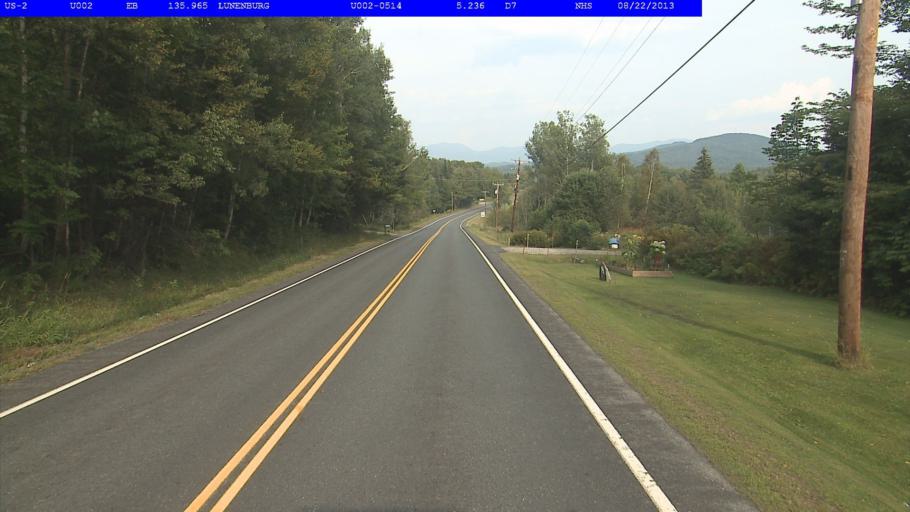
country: US
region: New Hampshire
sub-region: Coos County
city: Lancaster
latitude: 44.4639
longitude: -71.6715
